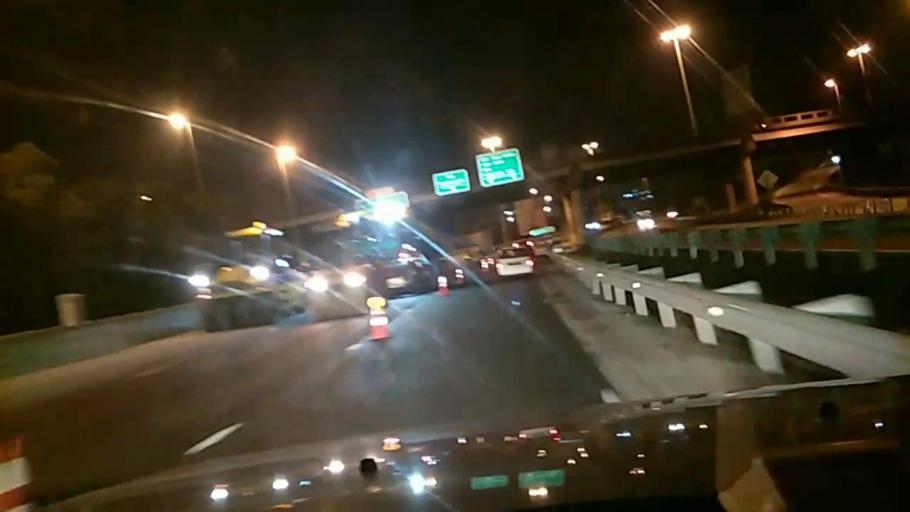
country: MY
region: Penang
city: Perai
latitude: 5.3636
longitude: 100.4004
